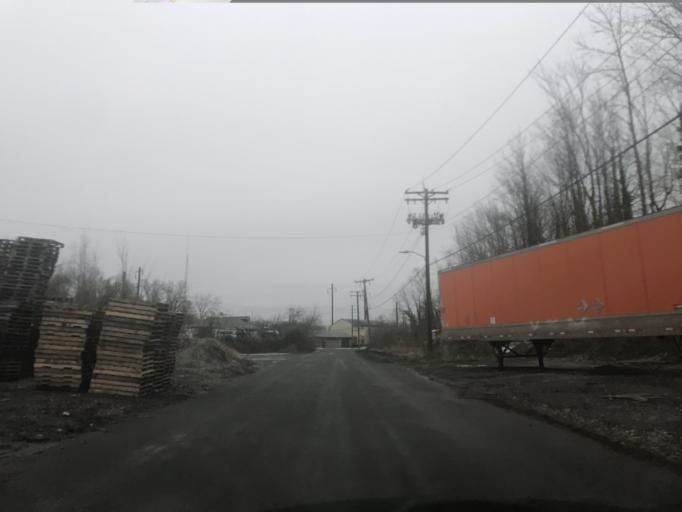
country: US
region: Maryland
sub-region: Baltimore County
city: Rossville
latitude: 39.3268
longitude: -76.4740
